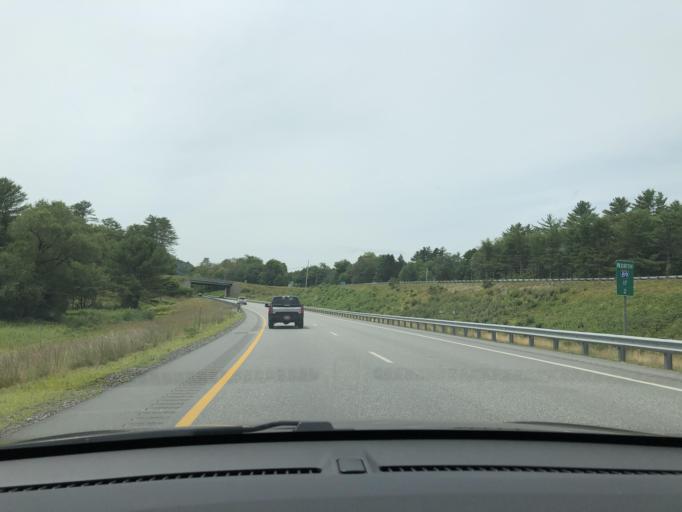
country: US
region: New Hampshire
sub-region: Merrimack County
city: Webster
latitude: 43.2735
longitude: -71.7899
